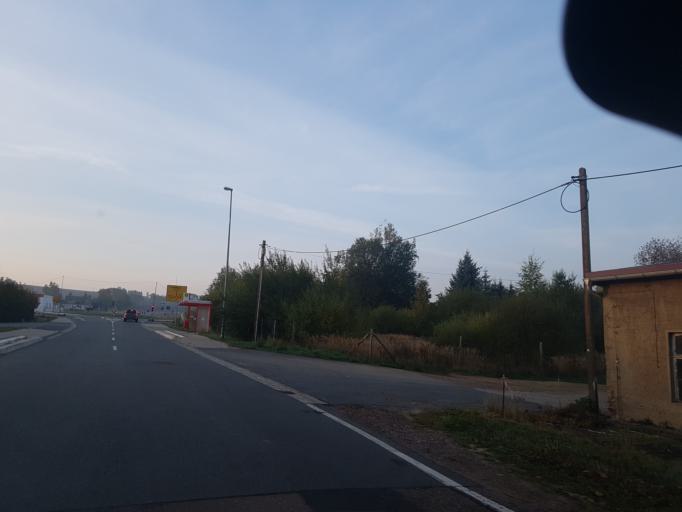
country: DE
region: Saxony
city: Grossweitzschen
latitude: 51.1276
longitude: 13.0544
